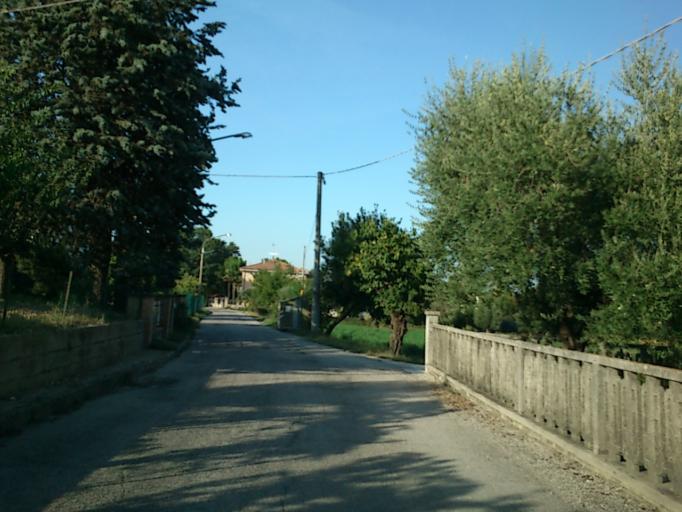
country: IT
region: The Marches
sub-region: Provincia di Pesaro e Urbino
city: Saltara
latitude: 43.7400
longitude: 12.9086
